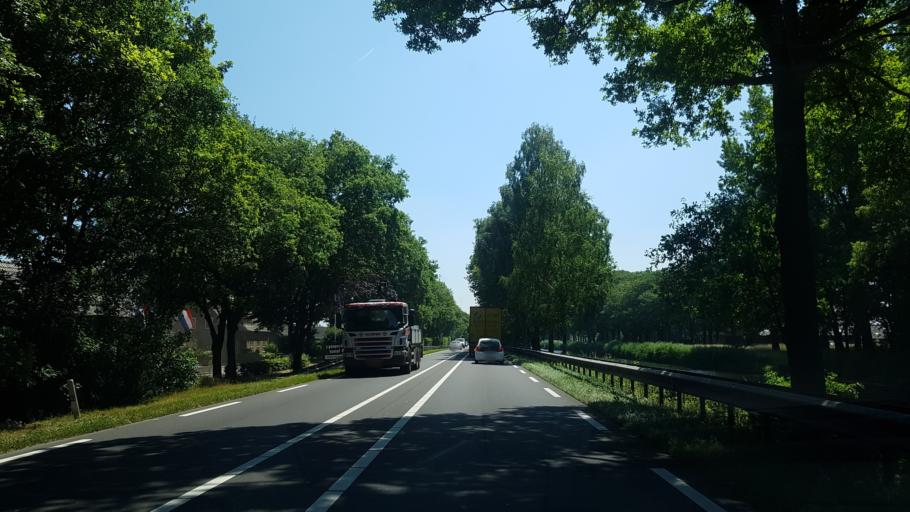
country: NL
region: North Brabant
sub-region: Gemeente Veghel
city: Keldonk
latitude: 51.5551
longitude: 5.6133
